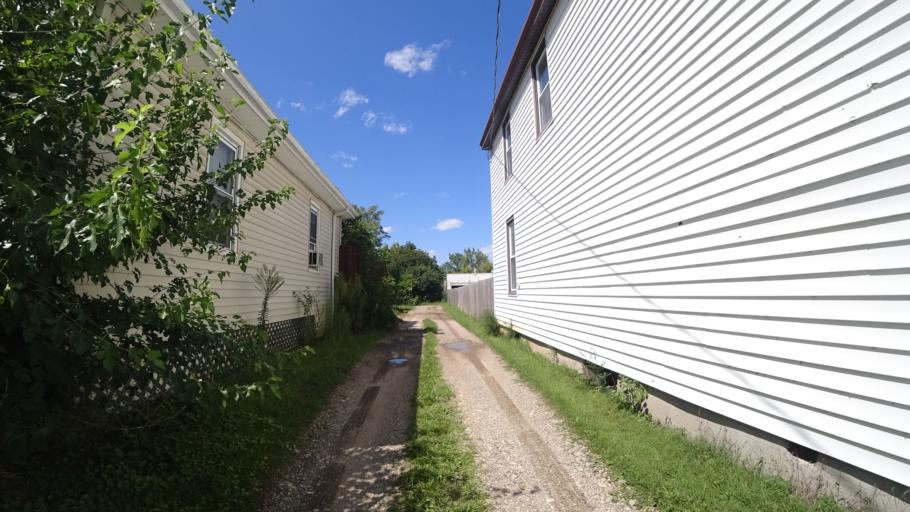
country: US
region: Ohio
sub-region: Butler County
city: Hamilton
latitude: 39.4053
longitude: -84.5429
